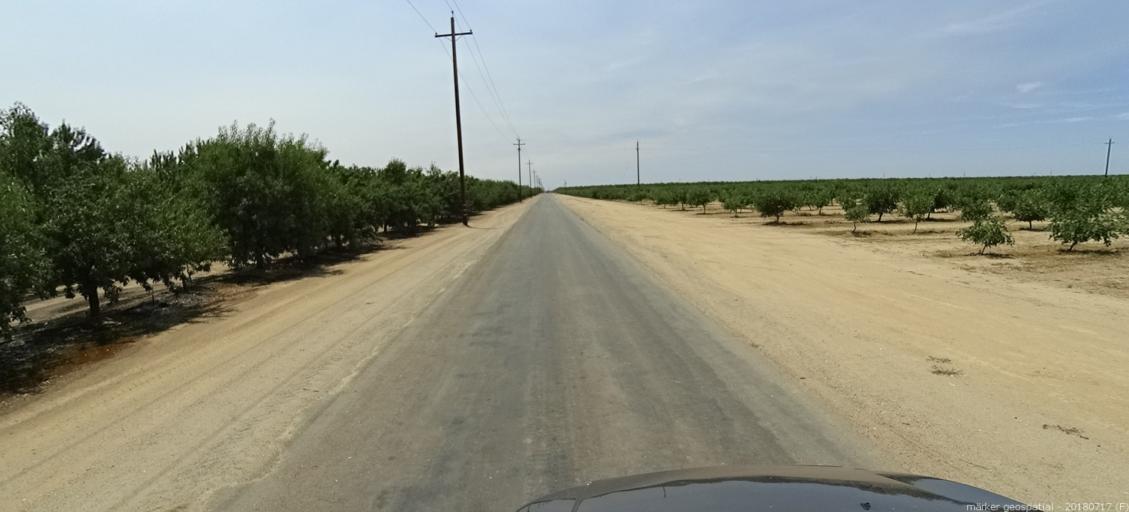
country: US
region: California
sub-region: Madera County
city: Fairmead
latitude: 37.1175
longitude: -120.1658
